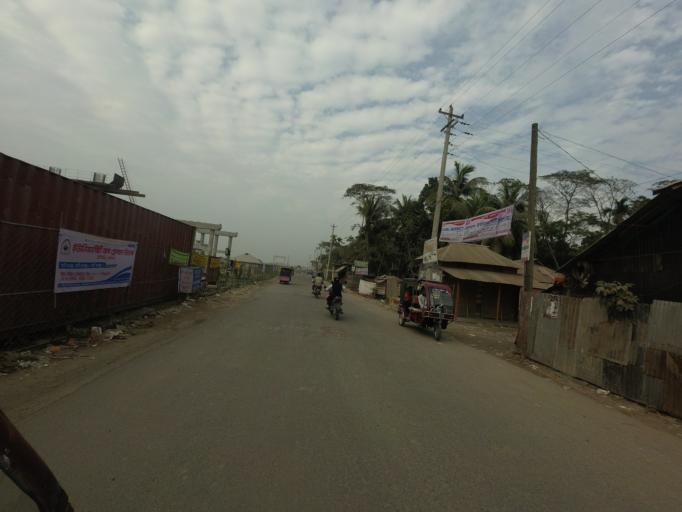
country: BD
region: Barisal
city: Nalchiti
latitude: 22.4611
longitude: 90.3414
